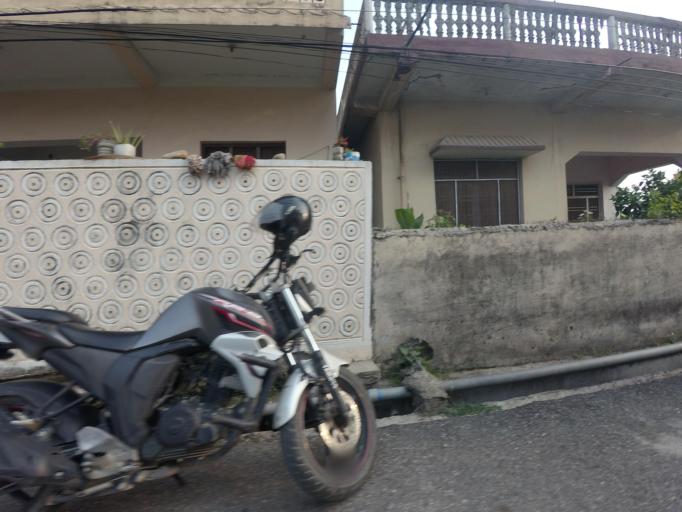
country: NP
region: Western Region
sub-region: Lumbini Zone
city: Bhairahawa
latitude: 27.5132
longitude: 83.4451
